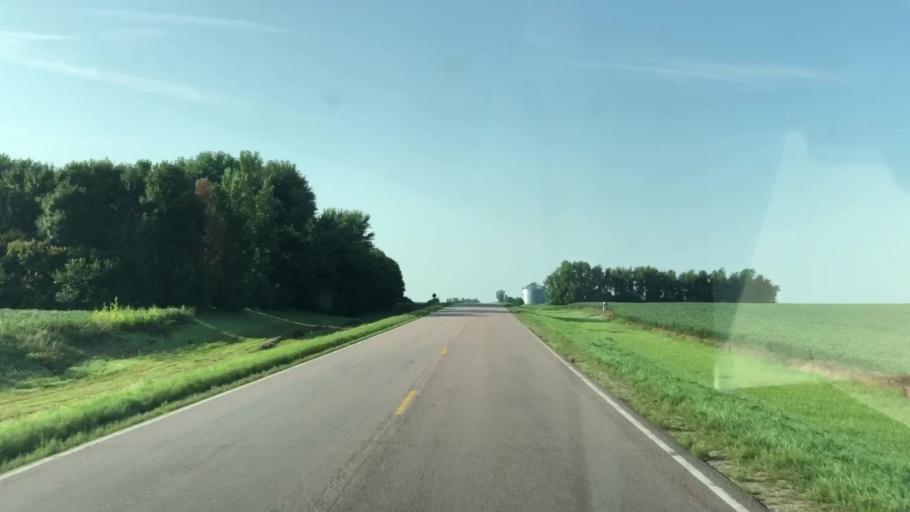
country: US
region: Iowa
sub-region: Lyon County
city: George
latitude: 43.3230
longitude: -95.9988
